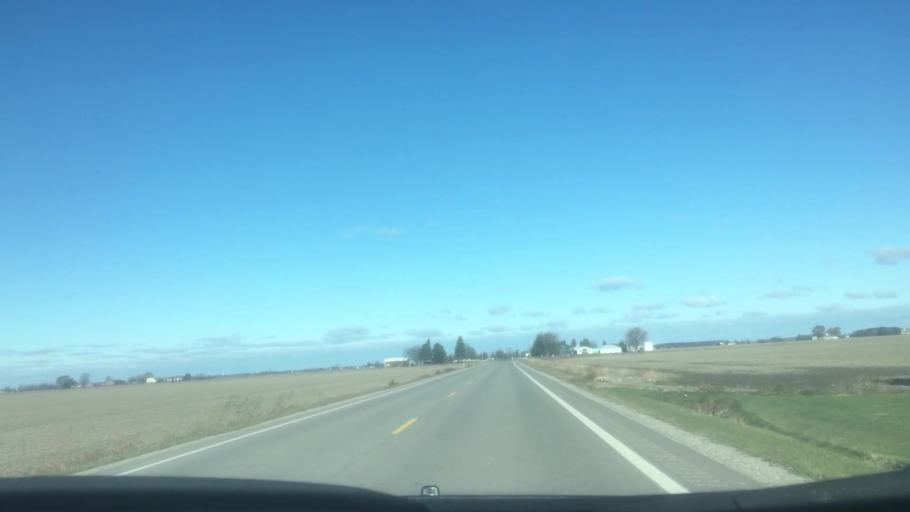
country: US
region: Michigan
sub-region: Tuscola County
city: Reese
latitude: 43.5255
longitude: -83.7587
